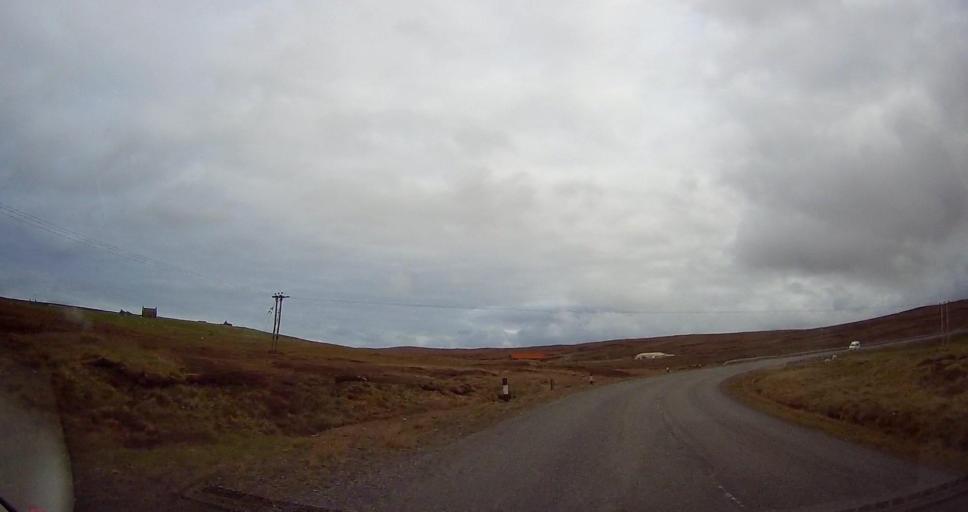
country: GB
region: Scotland
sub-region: Shetland Islands
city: Shetland
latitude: 60.6677
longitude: -1.0683
